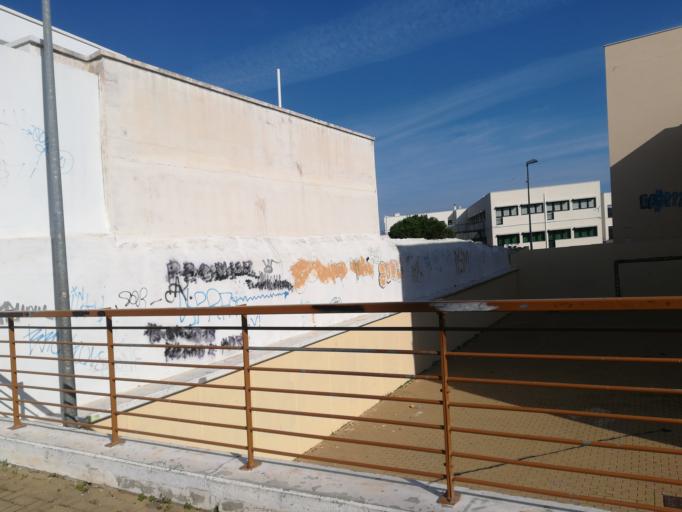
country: IT
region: Apulia
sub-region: Provincia di Bari
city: Polignano a Mare
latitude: 40.9936
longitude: 17.2253
